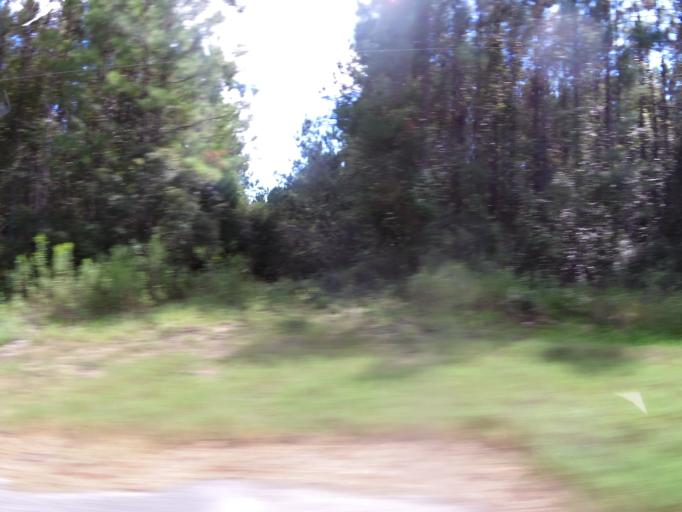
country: US
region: Florida
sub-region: Hamilton County
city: Jasper
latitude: 30.6251
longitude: -82.6105
